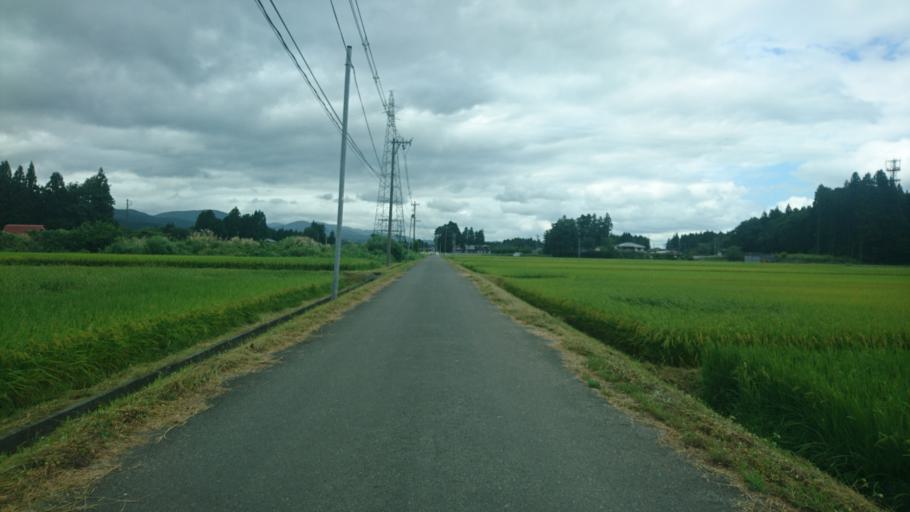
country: JP
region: Iwate
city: Kitakami
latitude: 39.3108
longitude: 140.9843
